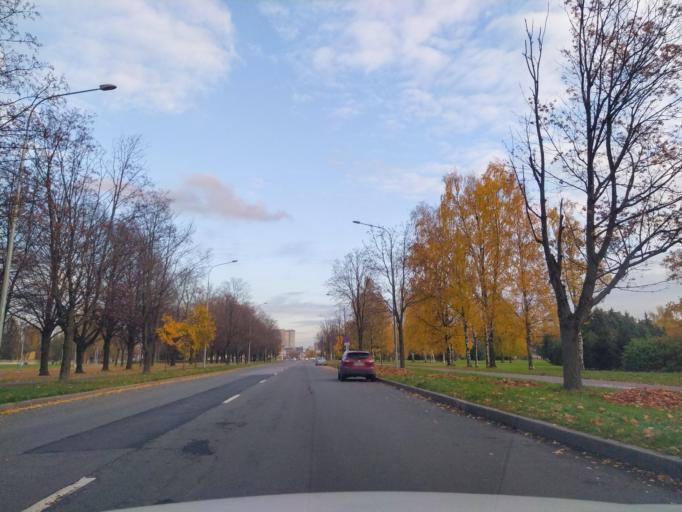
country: RU
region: Leningrad
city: Kalininskiy
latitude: 59.9816
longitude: 30.4151
